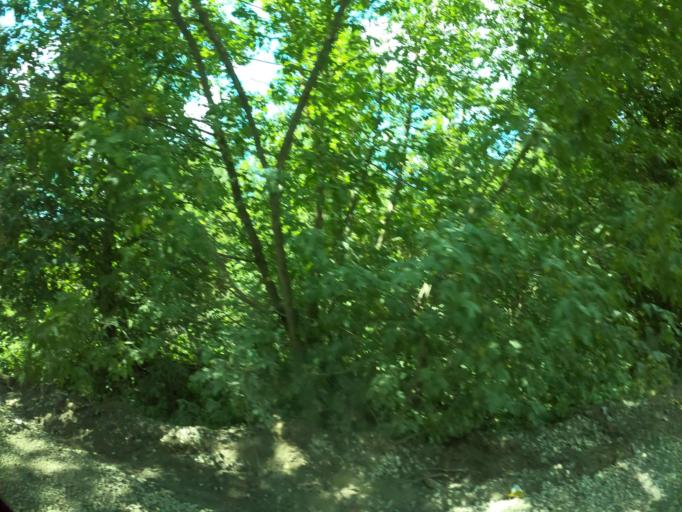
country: RU
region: Moskovskaya
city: Serpukhov
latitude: 54.9151
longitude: 37.3624
